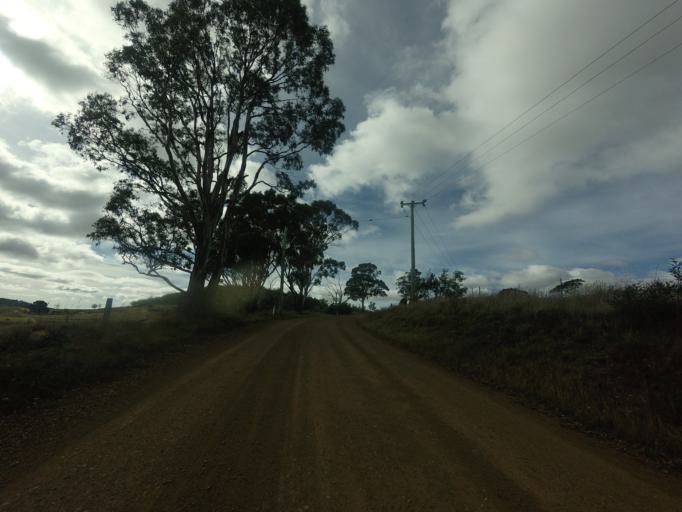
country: AU
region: Tasmania
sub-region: Brighton
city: Bridgewater
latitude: -42.3888
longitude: 147.4001
